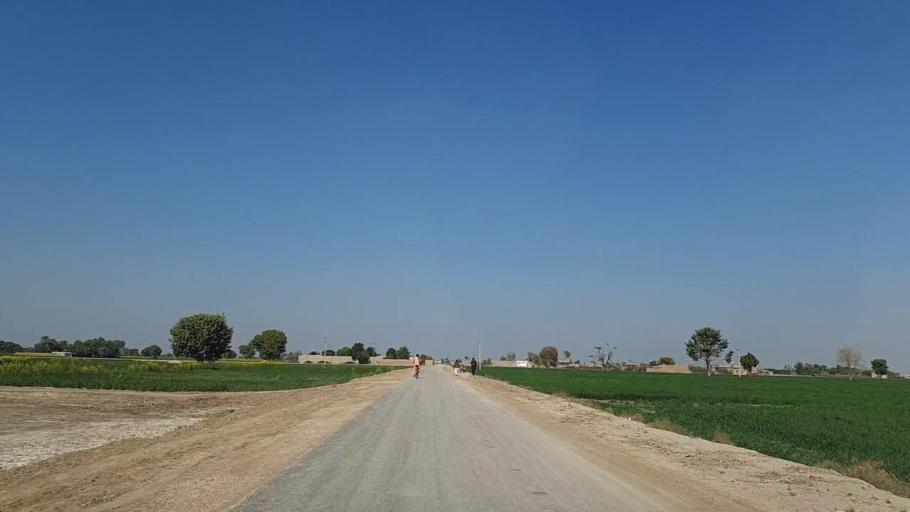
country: PK
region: Sindh
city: Nawabshah
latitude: 26.2470
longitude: 68.4512
